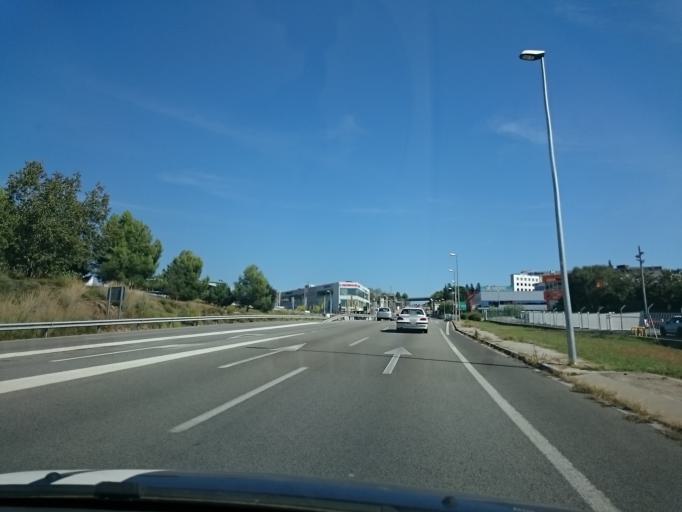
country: ES
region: Catalonia
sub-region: Provincia de Barcelona
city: Llica de Vall
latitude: 41.5931
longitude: 2.2624
